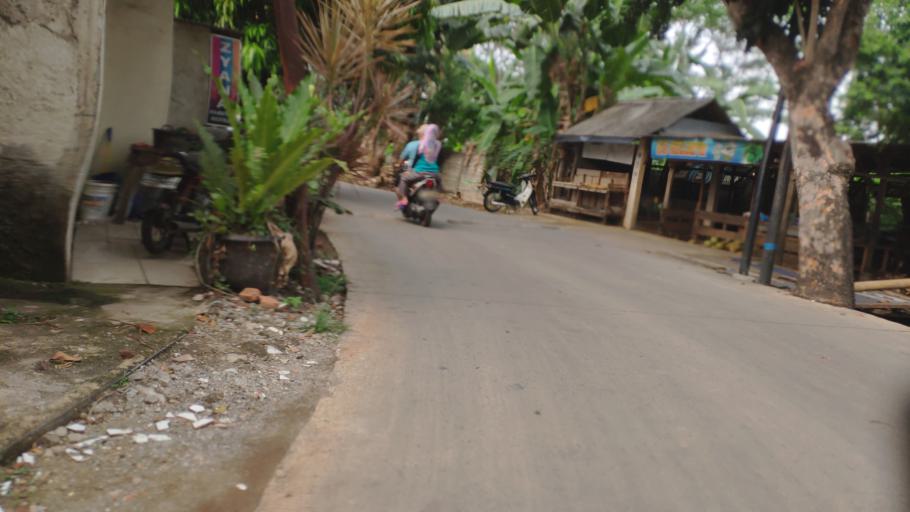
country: ID
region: West Java
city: Depok
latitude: -6.3393
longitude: 106.8135
